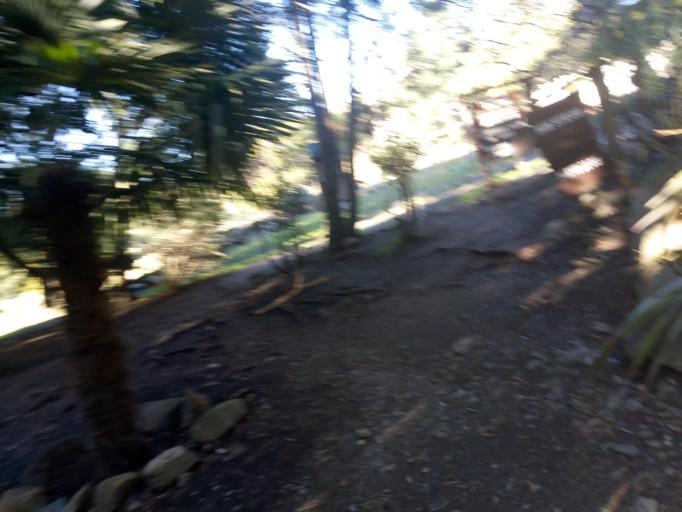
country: AR
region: Buenos Aires
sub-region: Partido de Tandil
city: Tandil
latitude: -37.3545
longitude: -59.1715
